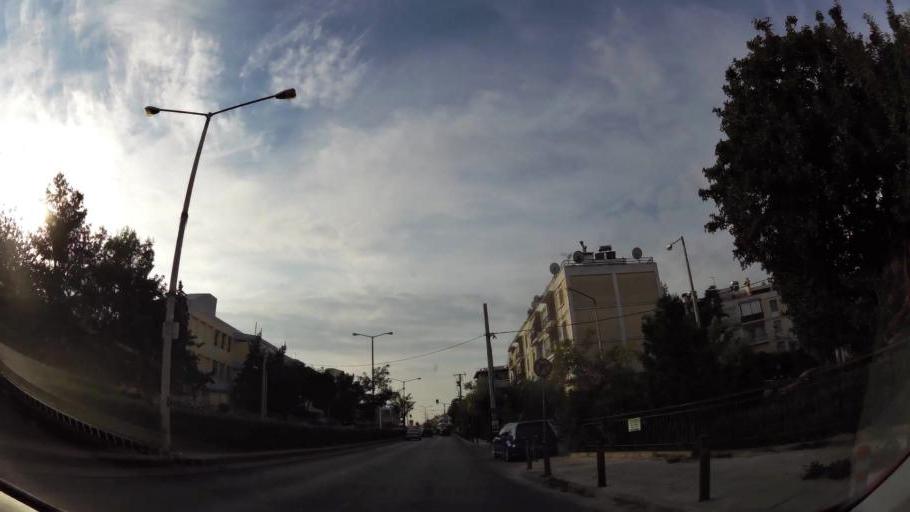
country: GR
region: Attica
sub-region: Nomarchia Athinas
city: Kallithea
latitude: 37.9403
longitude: 23.7007
